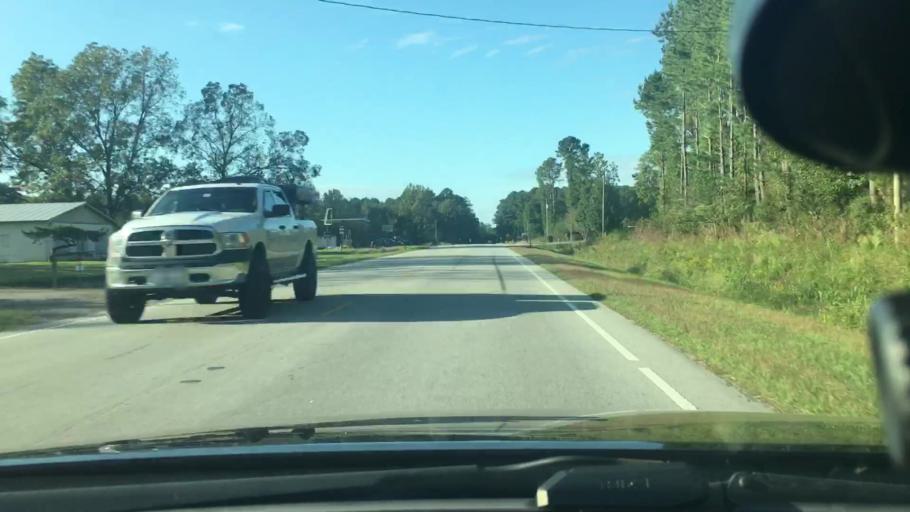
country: US
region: North Carolina
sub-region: Craven County
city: Vanceboro
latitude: 35.3158
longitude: -77.1421
